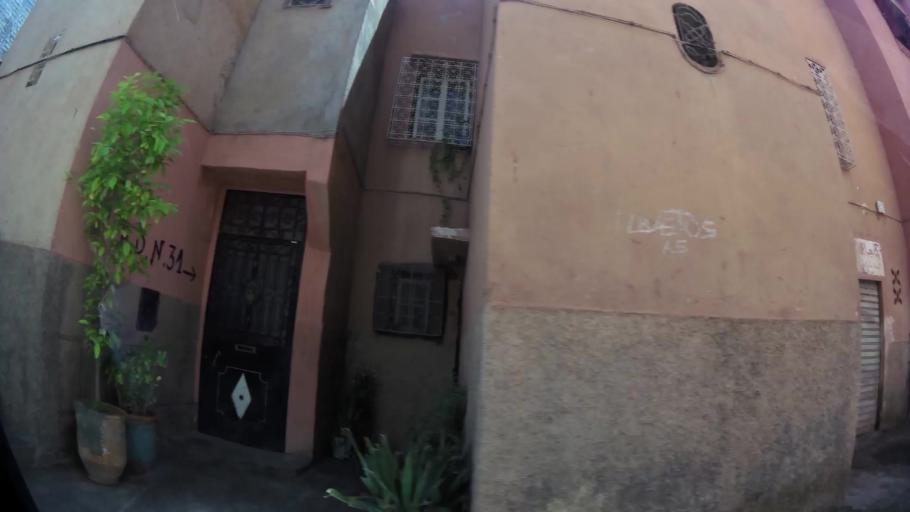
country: MA
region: Marrakech-Tensift-Al Haouz
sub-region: Marrakech
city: Marrakesh
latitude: 31.6535
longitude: -7.9943
